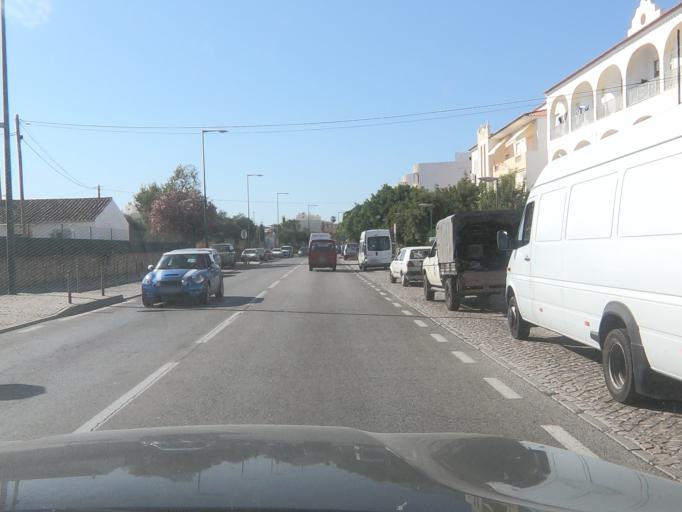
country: PT
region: Faro
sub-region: Loule
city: Loule
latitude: 37.1327
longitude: -8.0194
